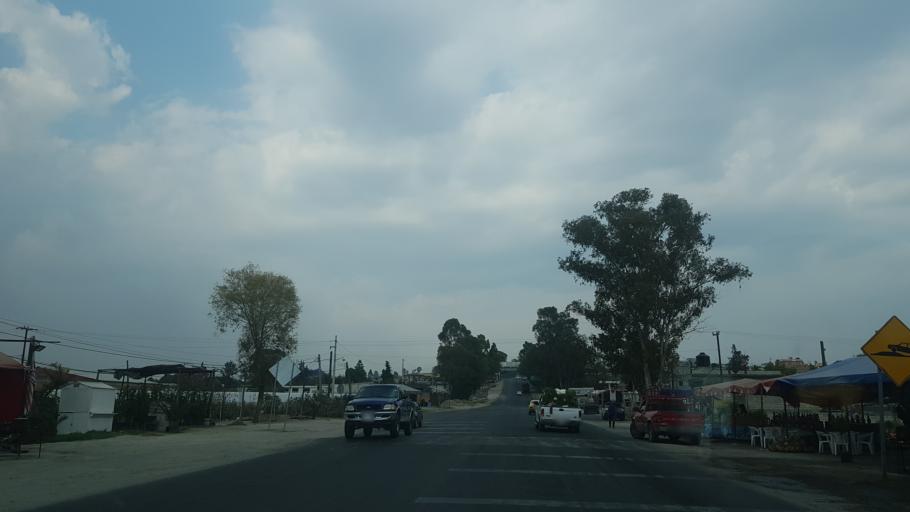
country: MX
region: Puebla
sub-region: Santa Isabel Cholula
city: San Pablo Ahuatempa
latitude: 18.9815
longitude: -98.3679
